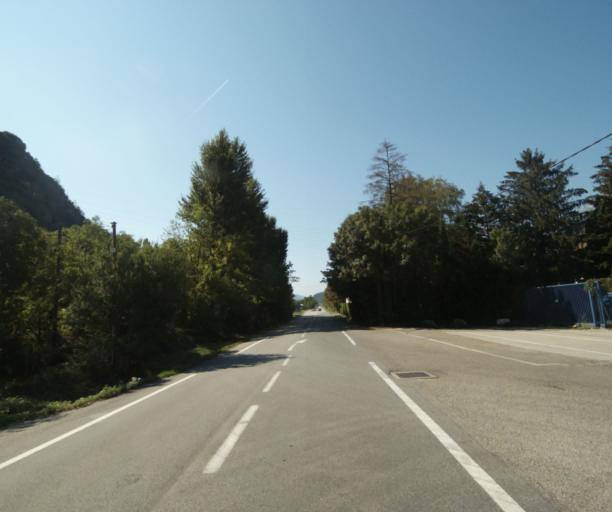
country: FR
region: Rhone-Alpes
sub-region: Departement de l'Isere
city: Allieres-et-Risset
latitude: 45.1100
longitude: 5.6885
